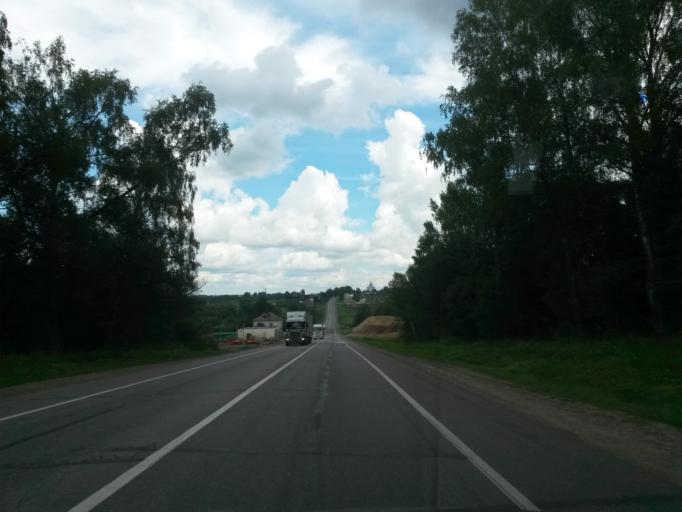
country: RU
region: Vladimir
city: Aleksandrov
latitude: 56.5905
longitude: 38.6149
